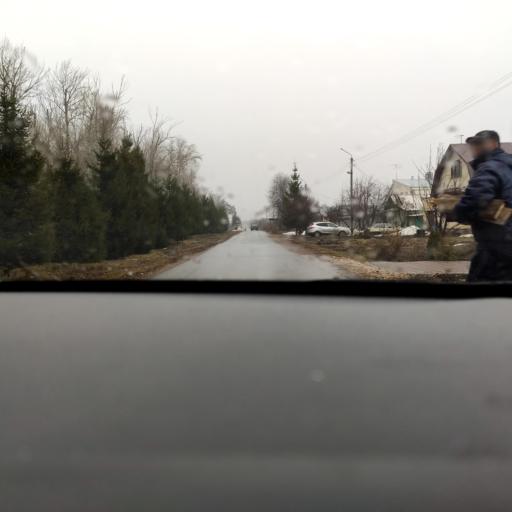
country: RU
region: Tatarstan
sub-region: Chistopol'skiy Rayon
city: Chistopol'
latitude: 55.3545
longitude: 50.6408
